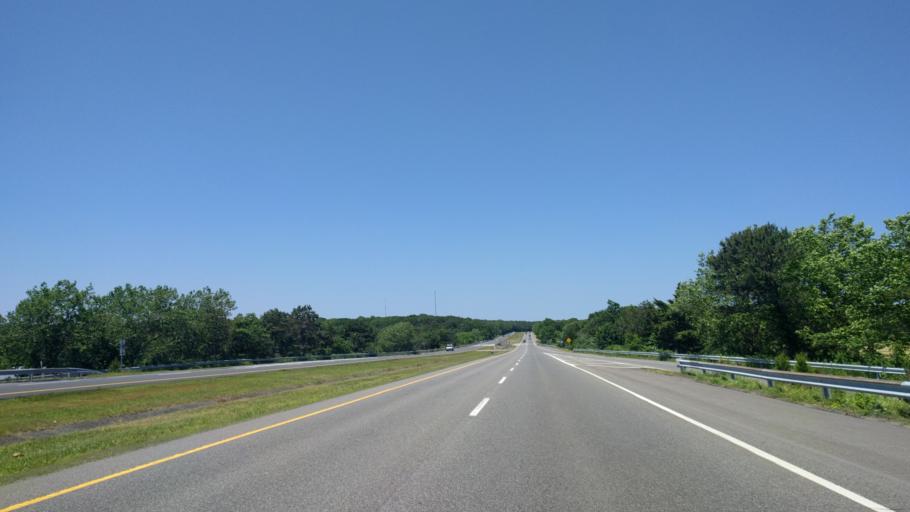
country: US
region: New York
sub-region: Suffolk County
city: Eastport
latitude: 40.8472
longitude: -72.7362
